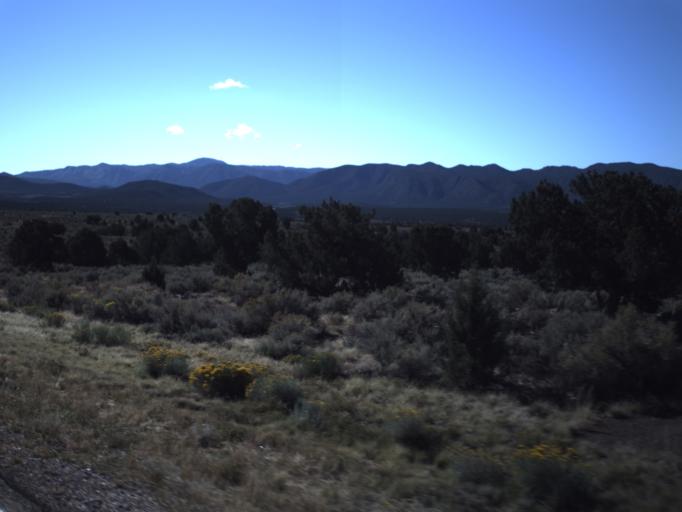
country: US
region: Utah
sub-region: Washington County
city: Enterprise
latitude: 37.6595
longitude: -113.4599
